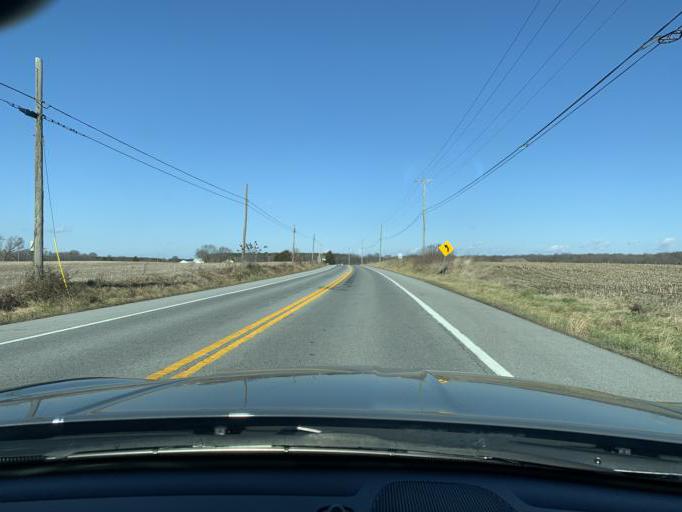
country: US
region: Maryland
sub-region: Queen Anne's County
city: Centreville
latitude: 39.0855
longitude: -76.0327
